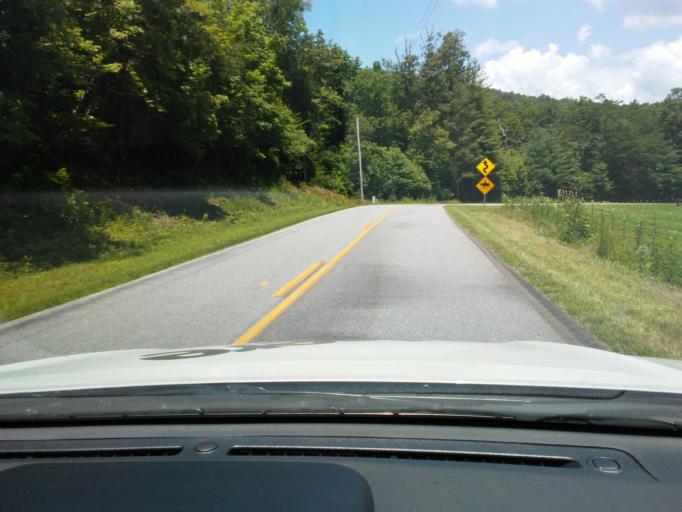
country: US
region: Georgia
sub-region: Towns County
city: Hiawassee
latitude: 34.8674
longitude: -83.7612
